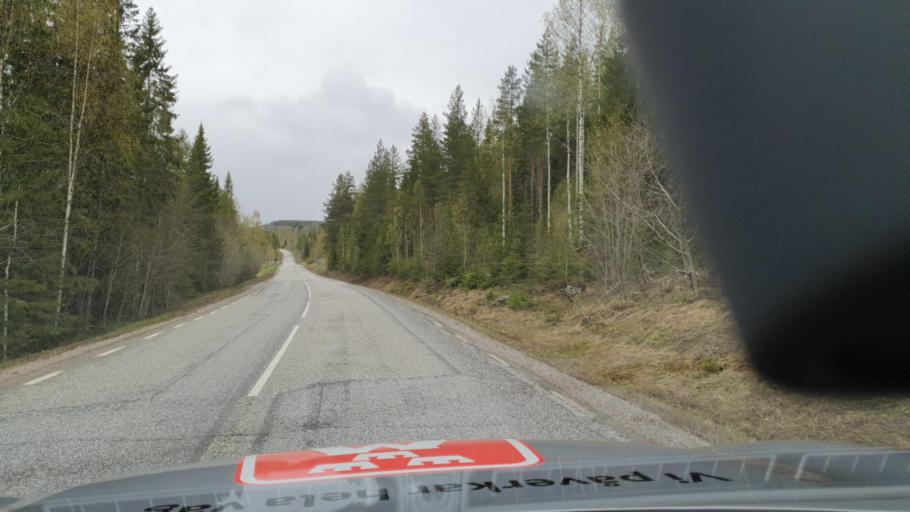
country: SE
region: Vaesterbotten
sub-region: Asele Kommun
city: Asele
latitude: 63.6722
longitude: 17.2558
